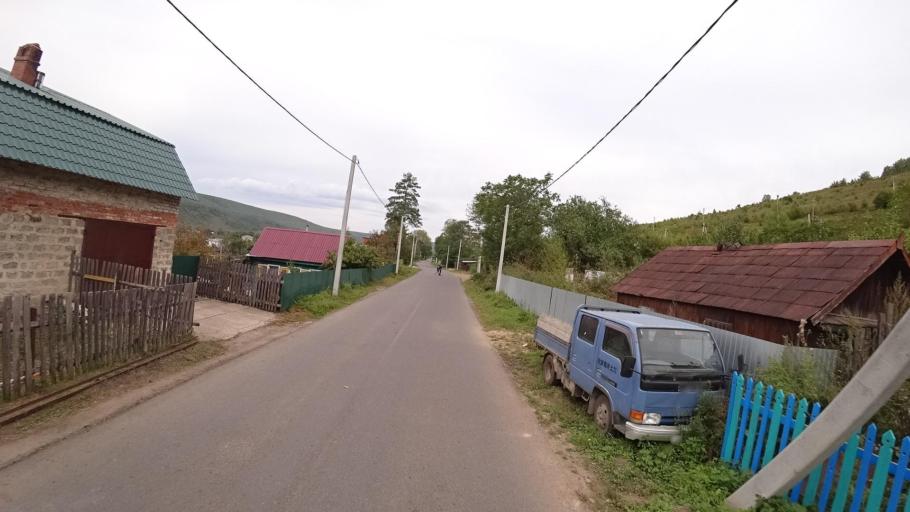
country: RU
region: Jewish Autonomous Oblast
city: Khingansk
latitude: 49.0253
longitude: 131.0592
